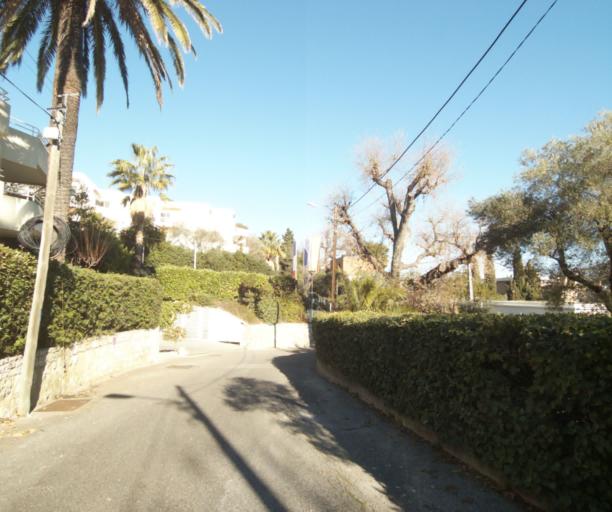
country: FR
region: Provence-Alpes-Cote d'Azur
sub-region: Departement des Alpes-Maritimes
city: Antibes
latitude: 43.5721
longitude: 7.1202
